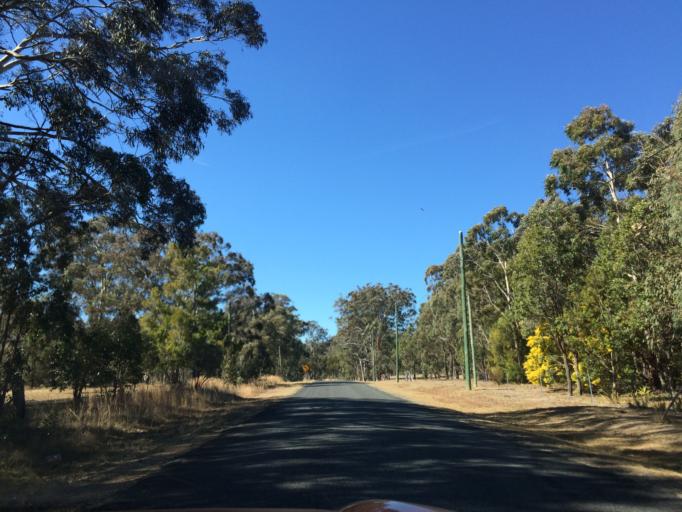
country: AU
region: Queensland
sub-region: Southern Downs
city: Stanthorpe
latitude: -28.6935
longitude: 152.0208
